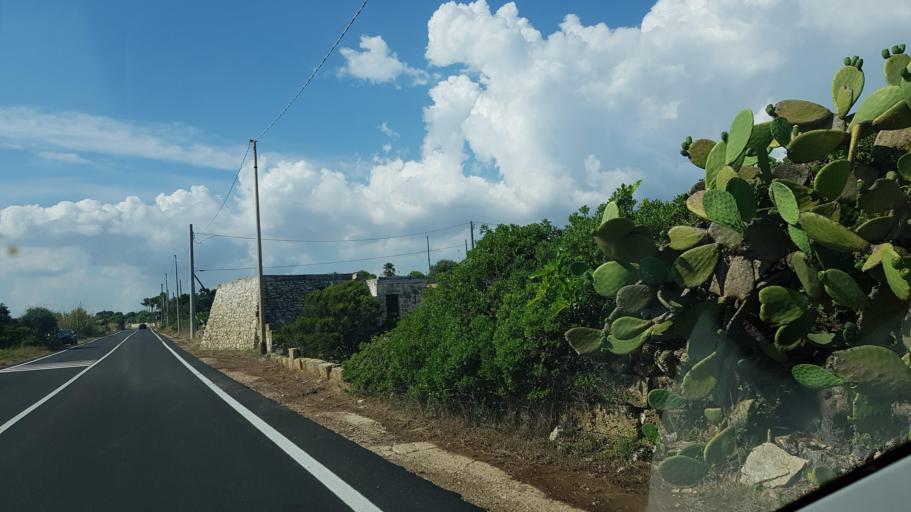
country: IT
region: Apulia
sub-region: Provincia di Lecce
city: Leuca
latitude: 39.7978
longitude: 18.3334
